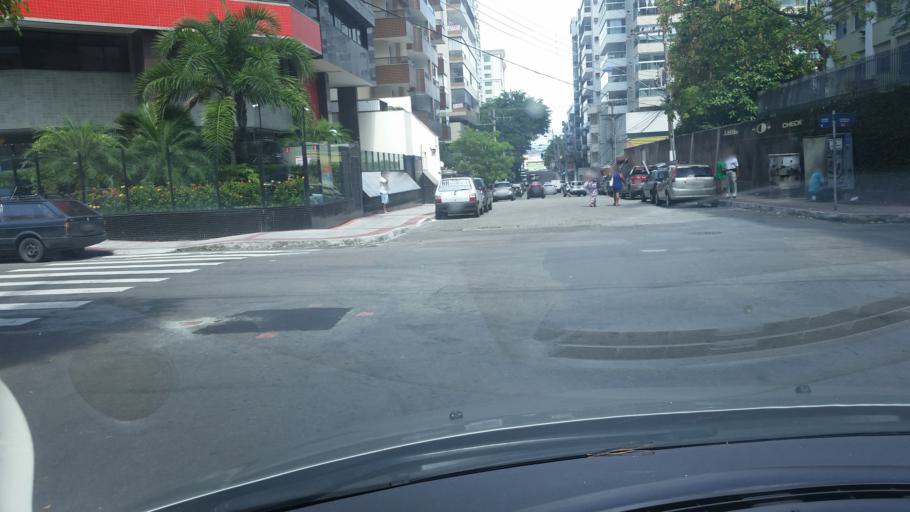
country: BR
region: Espirito Santo
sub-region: Vila Velha
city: Vila Velha
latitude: -20.3431
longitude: -40.2862
